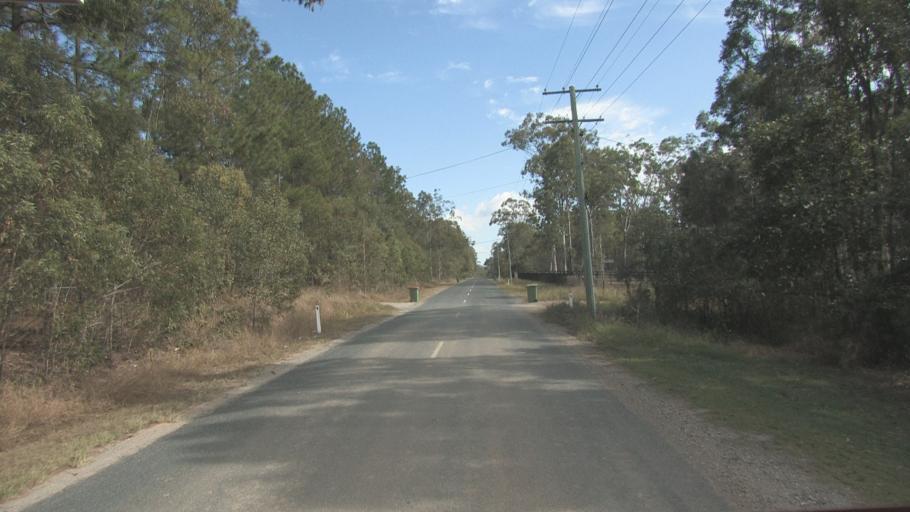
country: AU
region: Queensland
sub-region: Logan
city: North Maclean
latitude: -27.7605
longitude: 152.9817
